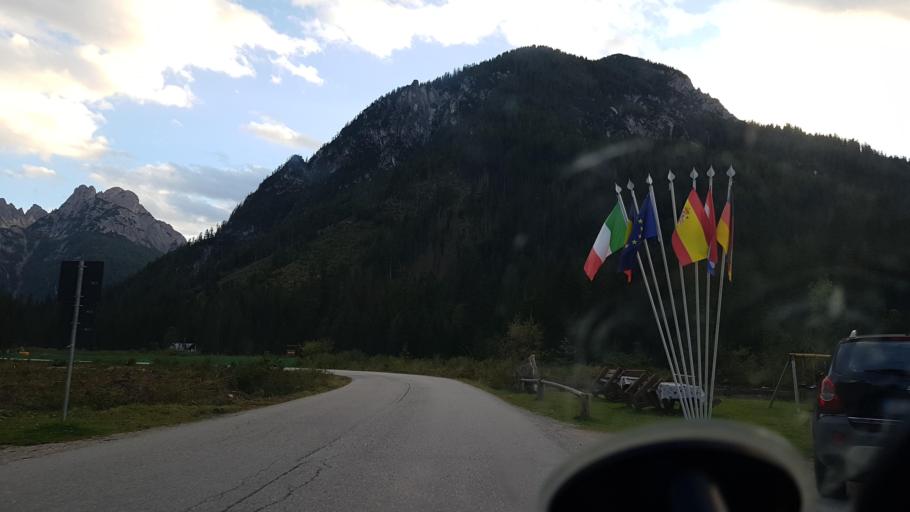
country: IT
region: Veneto
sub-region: Provincia di Belluno
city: San Pietro di Cadore
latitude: 46.6076
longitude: 12.6301
